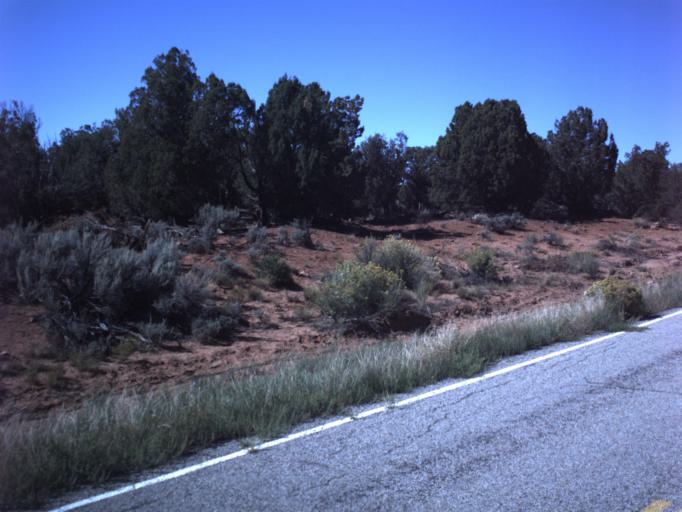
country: US
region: Utah
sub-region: San Juan County
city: Blanding
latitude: 37.5013
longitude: -109.8946
